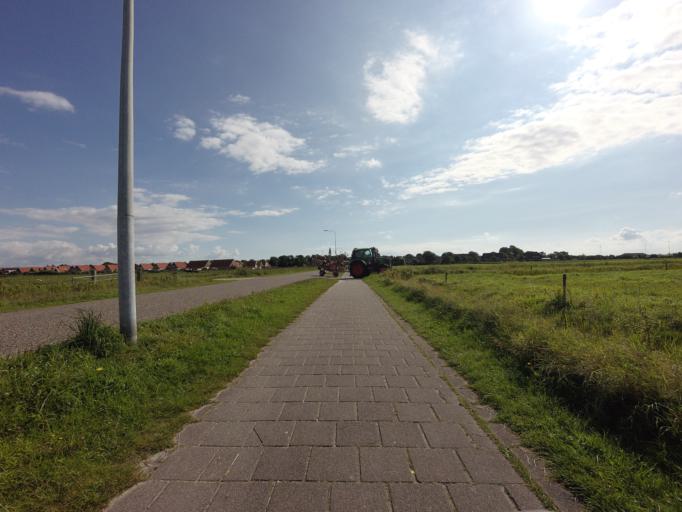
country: NL
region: Friesland
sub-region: Gemeente Terschelling
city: West-Terschelling
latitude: 53.3868
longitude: 5.2847
